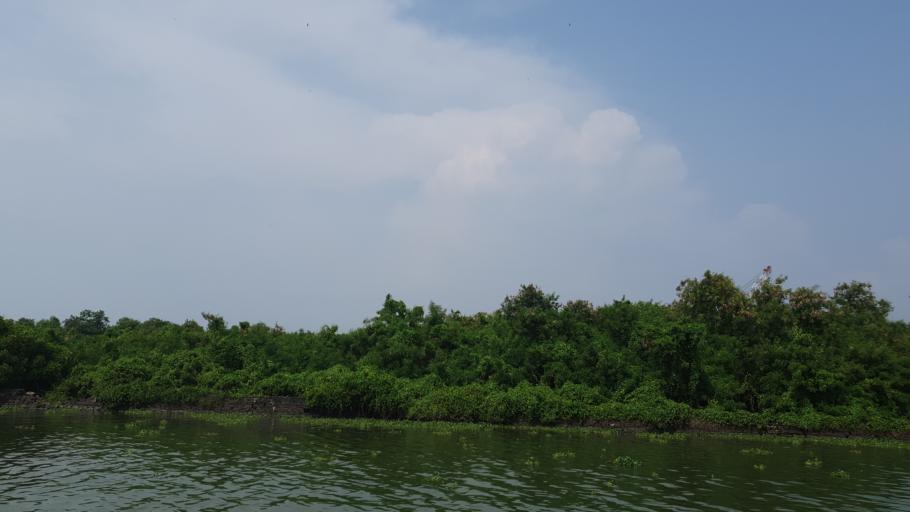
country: IN
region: Kerala
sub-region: Ernakulam
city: Cochin
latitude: 9.9759
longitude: 76.2480
